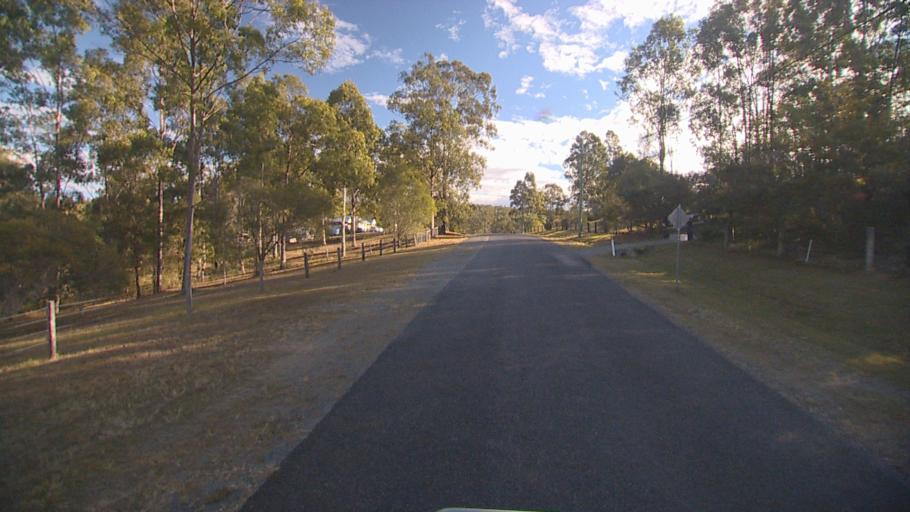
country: AU
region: Queensland
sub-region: Logan
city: Cedar Vale
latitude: -27.9310
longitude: 153.0639
